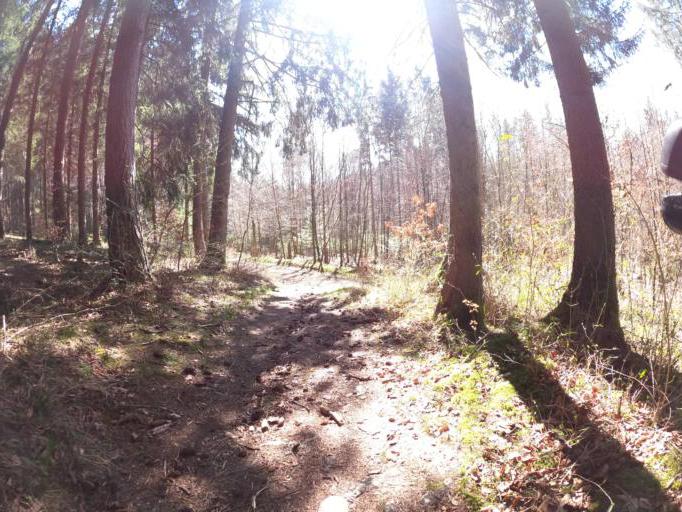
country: DE
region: Baden-Wuerttemberg
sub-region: Karlsruhe Region
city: Horb am Neckar
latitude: 48.4150
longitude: 8.6849
